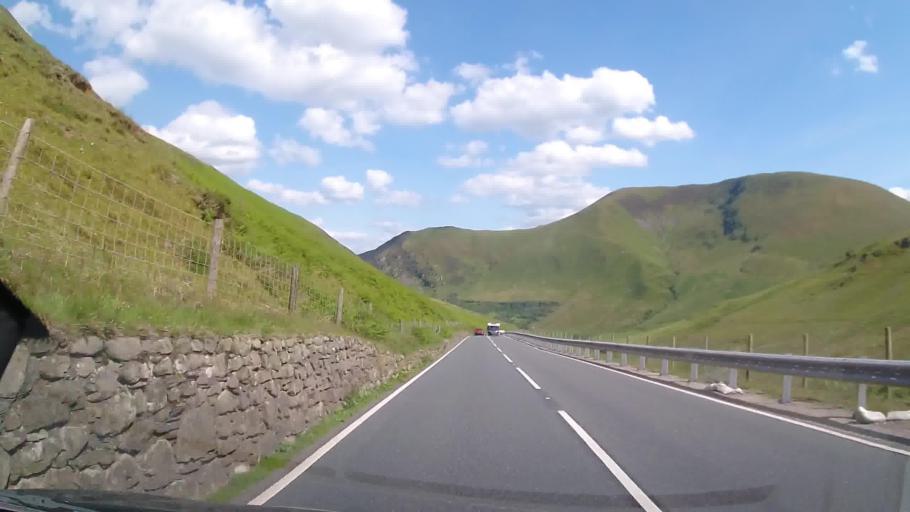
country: GB
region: Wales
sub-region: Gwynedd
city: Corris
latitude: 52.7354
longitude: -3.7669
